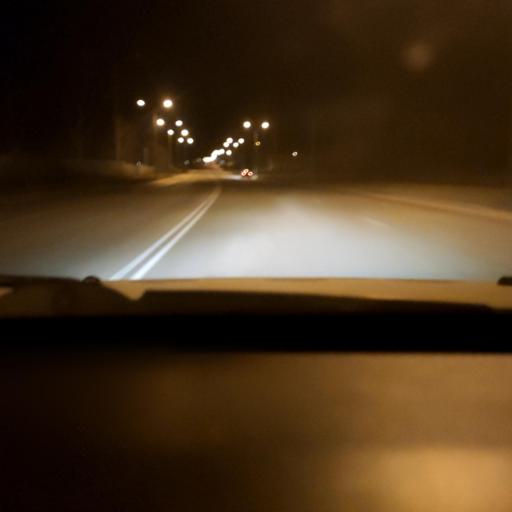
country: RU
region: Perm
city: Perm
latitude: 58.1112
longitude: 56.3993
